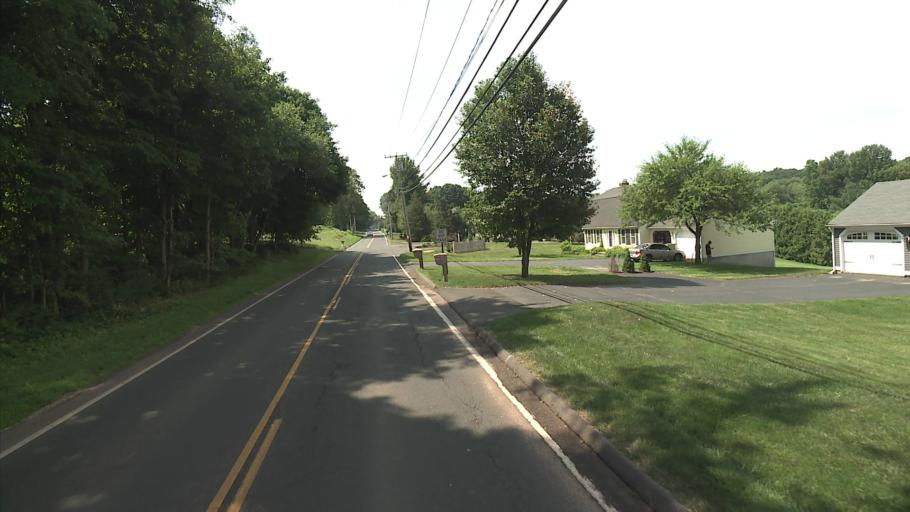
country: US
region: Connecticut
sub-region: Middlesex County
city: Cromwell
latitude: 41.5883
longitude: -72.6999
